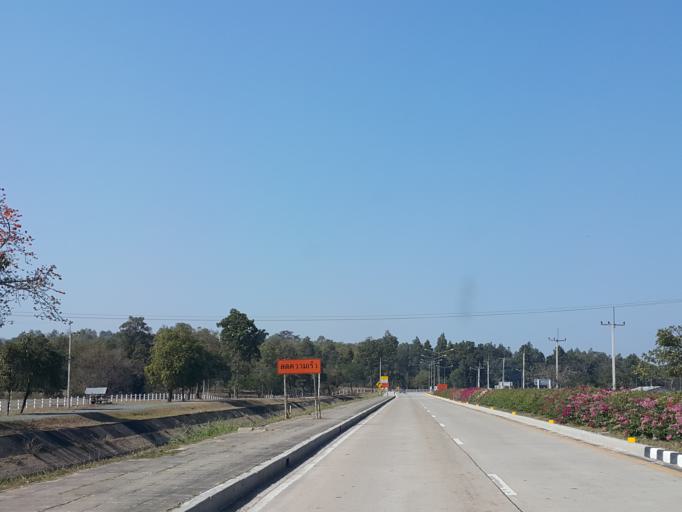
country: TH
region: Chiang Mai
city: Chiang Mai
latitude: 18.8622
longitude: 98.9601
